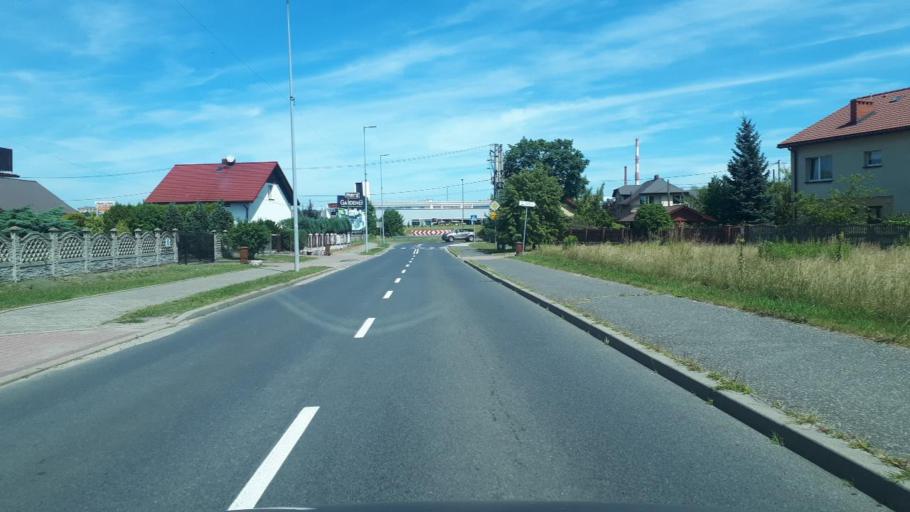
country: PL
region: Silesian Voivodeship
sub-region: Tychy
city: Cielmice
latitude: 50.0904
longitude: 19.0086
